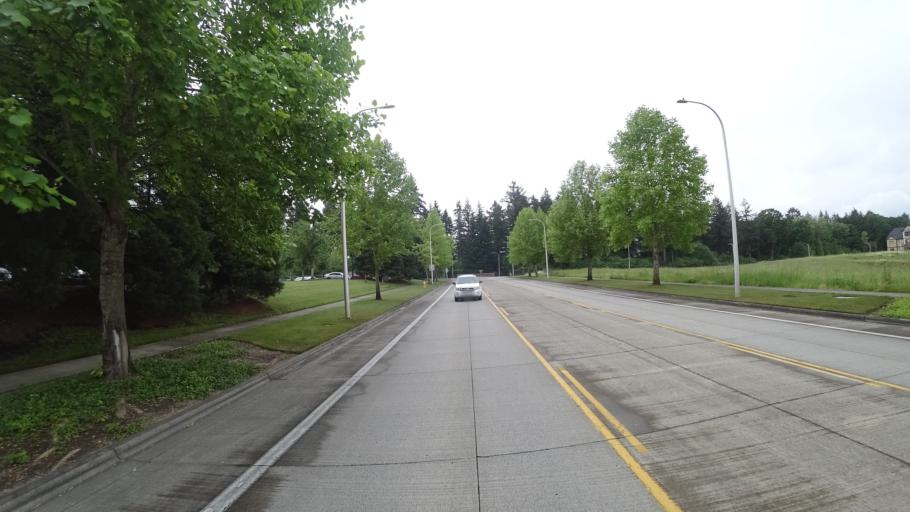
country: US
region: Oregon
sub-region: Washington County
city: Rockcreek
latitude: 45.5280
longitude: -122.8843
